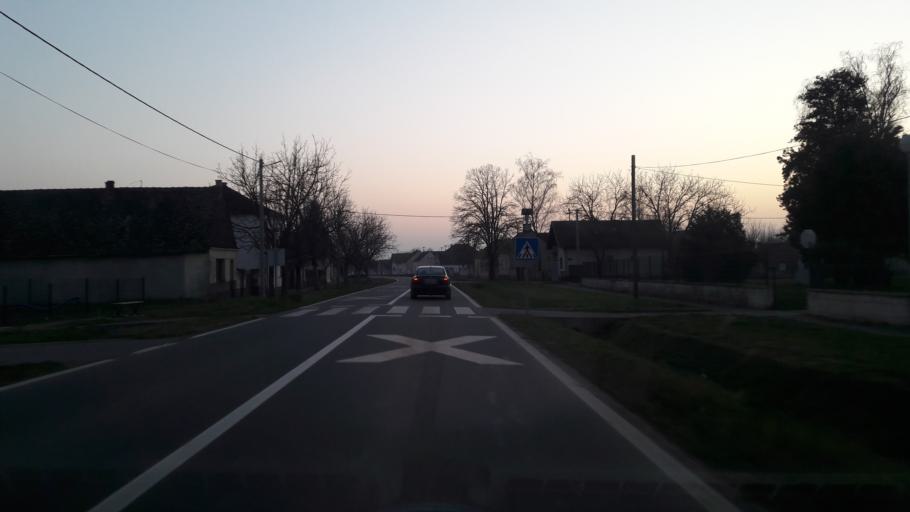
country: HR
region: Vukovarsko-Srijemska
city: Slakovci
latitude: 45.2212
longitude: 18.9876
